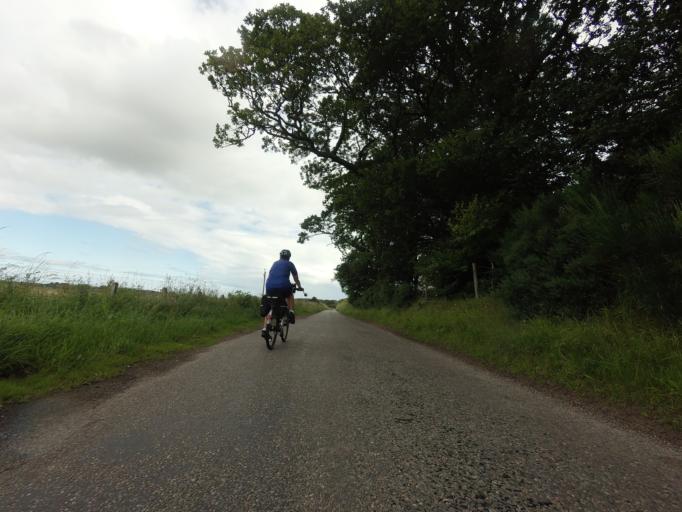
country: GB
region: Scotland
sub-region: Moray
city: Lhanbryd
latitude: 57.6482
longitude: -3.2423
